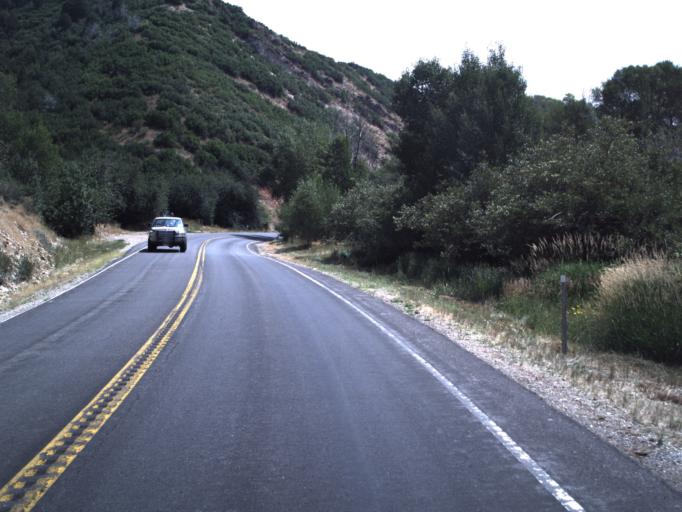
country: US
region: Utah
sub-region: Summit County
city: Francis
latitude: 40.5679
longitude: -111.1956
